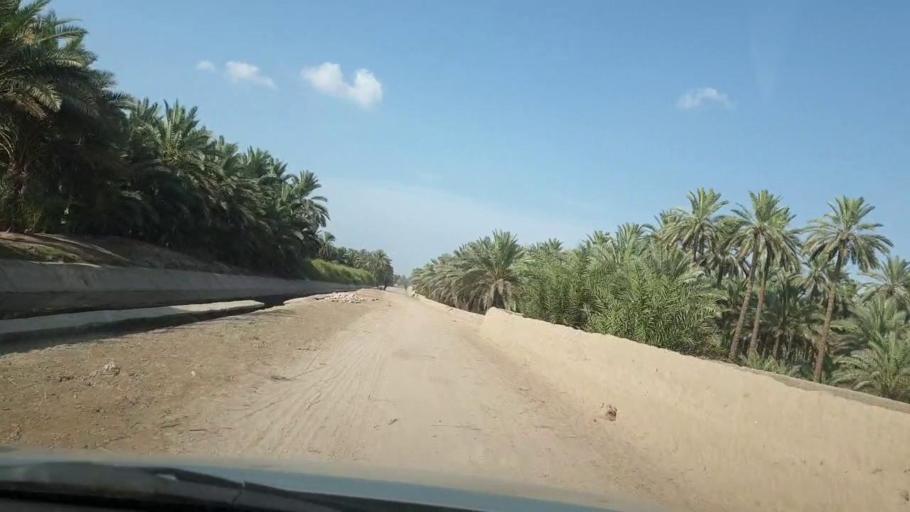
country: PK
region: Sindh
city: Sukkur
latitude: 27.6472
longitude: 68.8240
